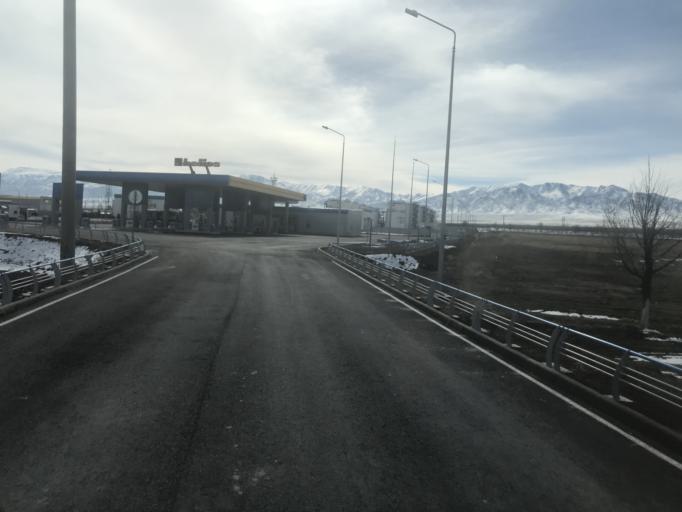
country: KZ
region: Zhambyl
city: Sarykemer
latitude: 43.0091
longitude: 71.7845
